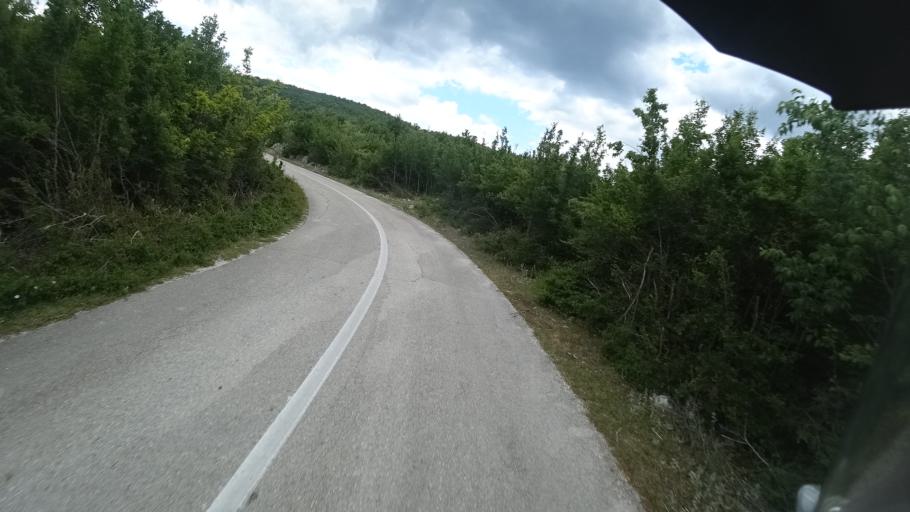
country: HR
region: Zadarska
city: Gracac
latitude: 44.1931
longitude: 15.8880
